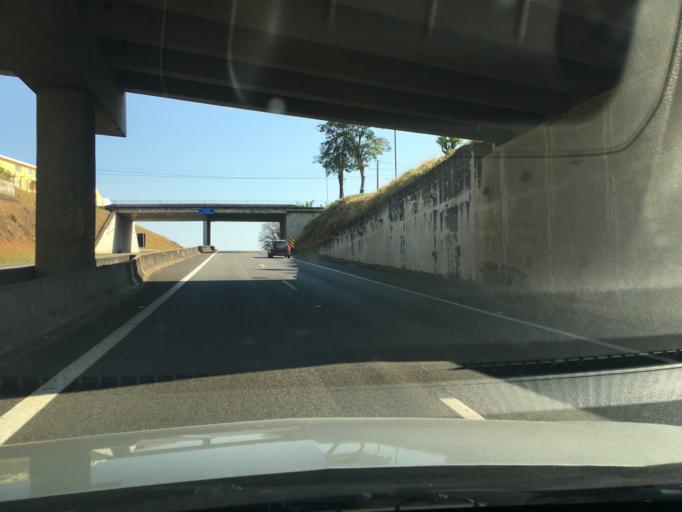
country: BR
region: Sao Paulo
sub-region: Sao Joao Da Boa Vista
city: Sao Joao da Boa Vista
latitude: -21.9850
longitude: -46.7885
